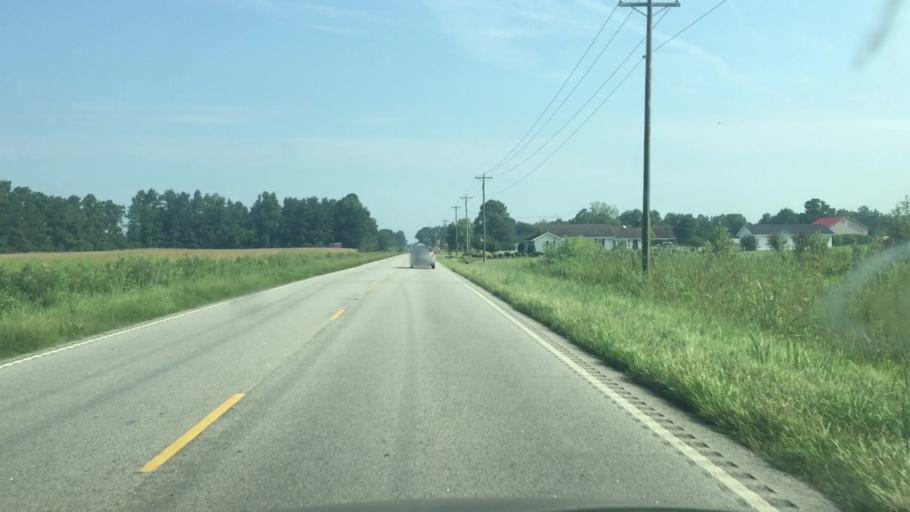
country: US
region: North Carolina
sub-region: Columbus County
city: Tabor City
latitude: 34.1260
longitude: -78.8759
